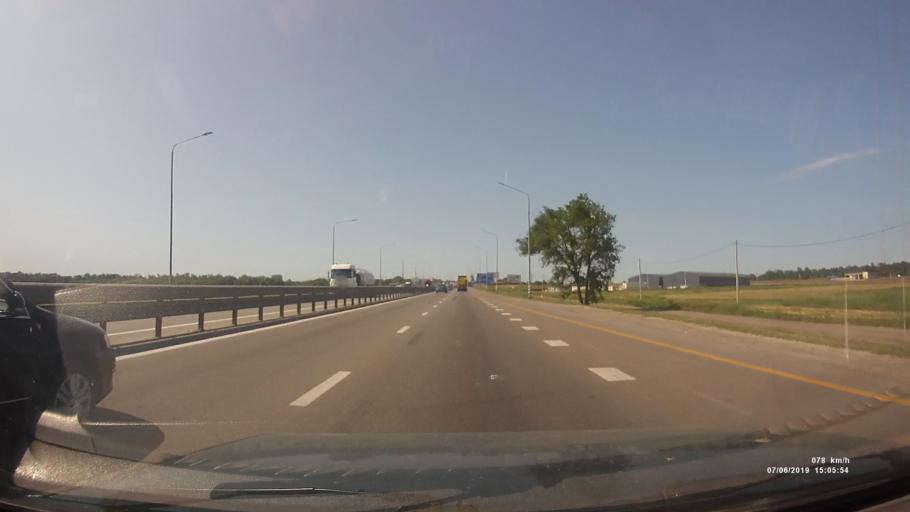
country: RU
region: Rostov
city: Aksay
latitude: 47.2779
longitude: 39.8520
